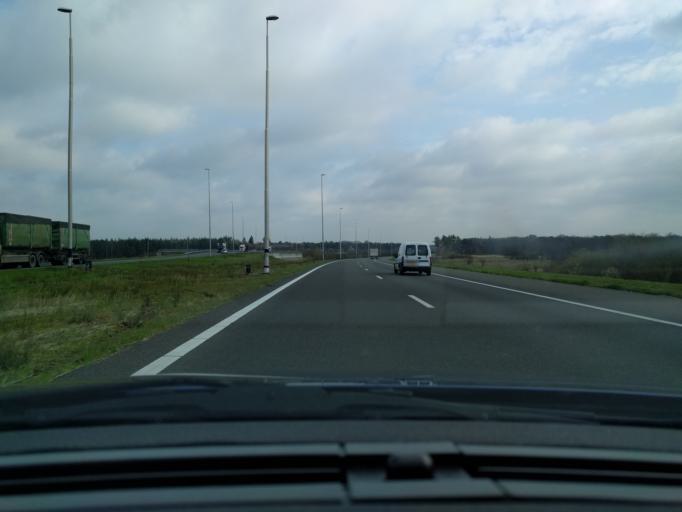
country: NL
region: North Brabant
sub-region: Gemeente Oss
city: Berghem
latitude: 51.7349
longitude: 5.5783
